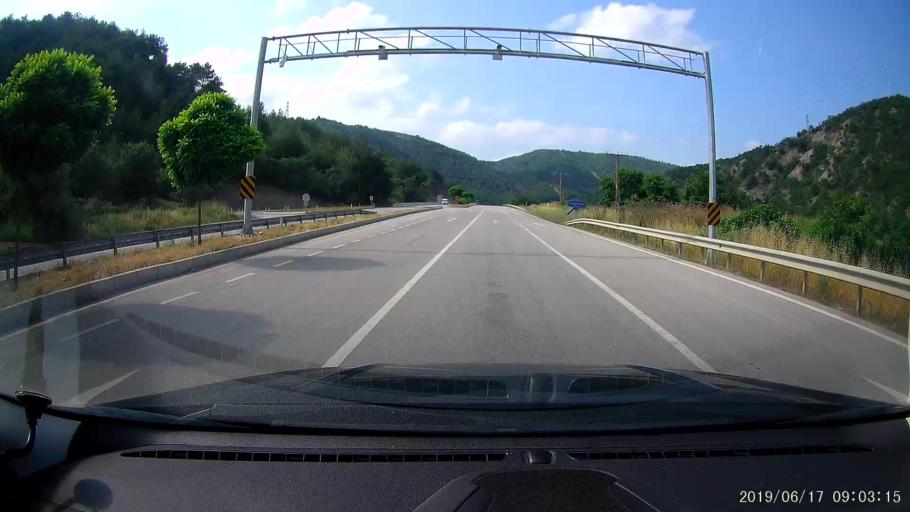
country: TR
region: Amasya
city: Tasova
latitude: 40.7580
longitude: 36.3023
